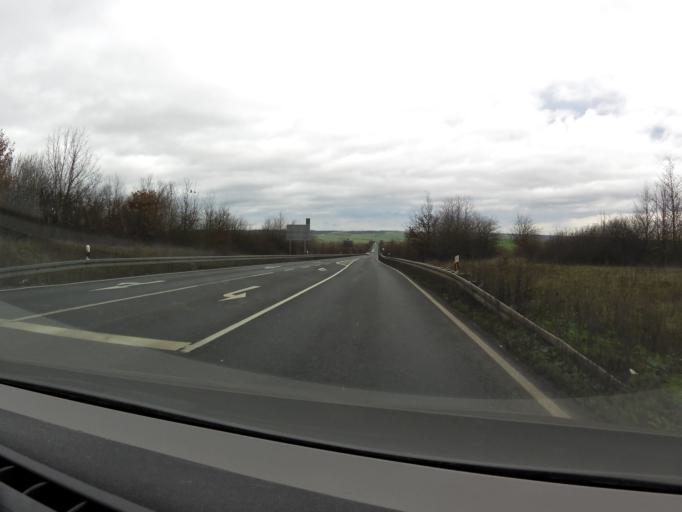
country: DE
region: Saxony-Anhalt
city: Sangerhausen
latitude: 51.4693
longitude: 11.3288
